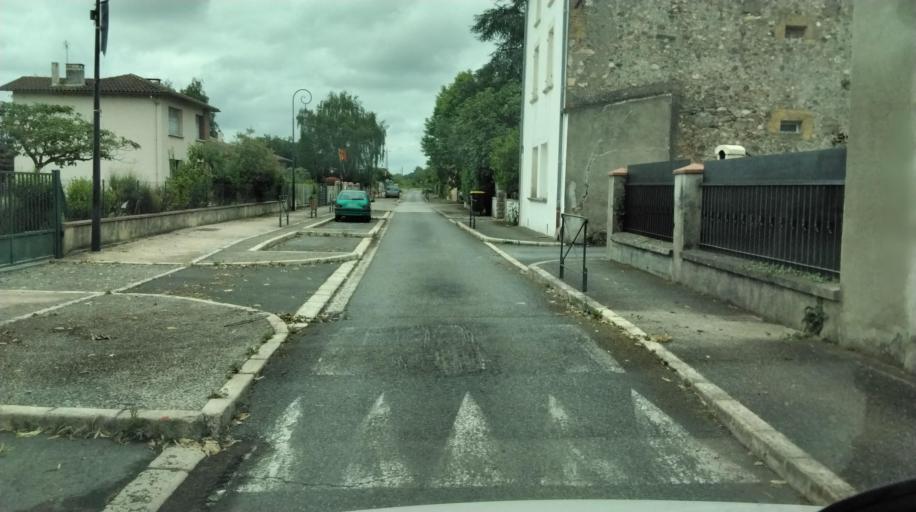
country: FR
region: Midi-Pyrenees
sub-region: Departement de la Haute-Garonne
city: Martres-Tolosane
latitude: 43.1972
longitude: 1.0155
